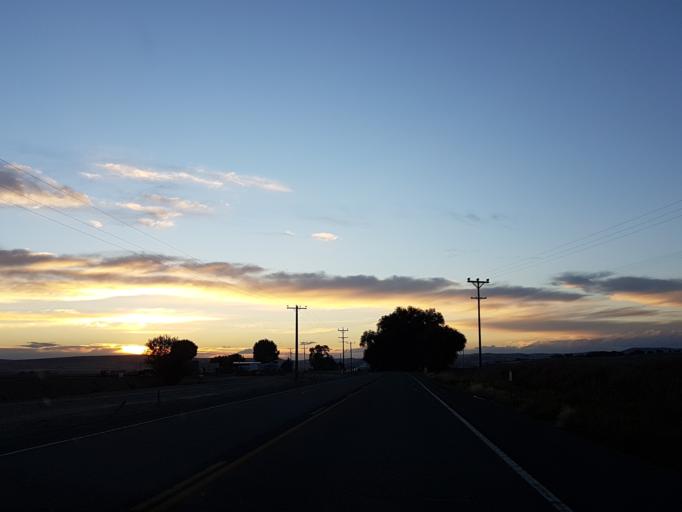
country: US
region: Oregon
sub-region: Malheur County
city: Vale
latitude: 43.9386
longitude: -117.3309
